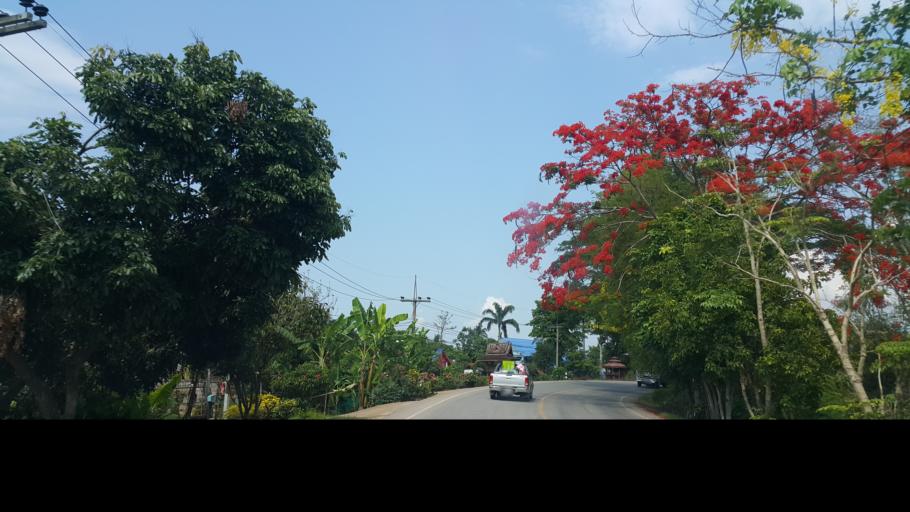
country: TH
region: Chiang Rai
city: Wiang Chai
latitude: 20.0103
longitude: 99.9149
